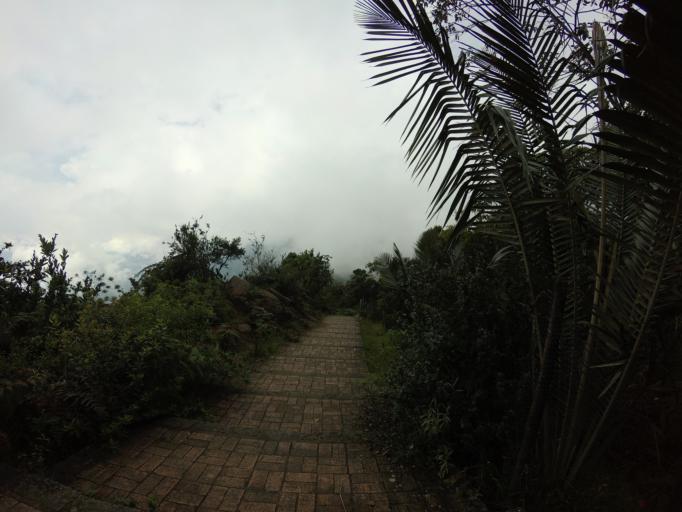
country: CO
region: Cundinamarca
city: San Antonio del Tequendama
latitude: 4.6069
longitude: -74.3070
